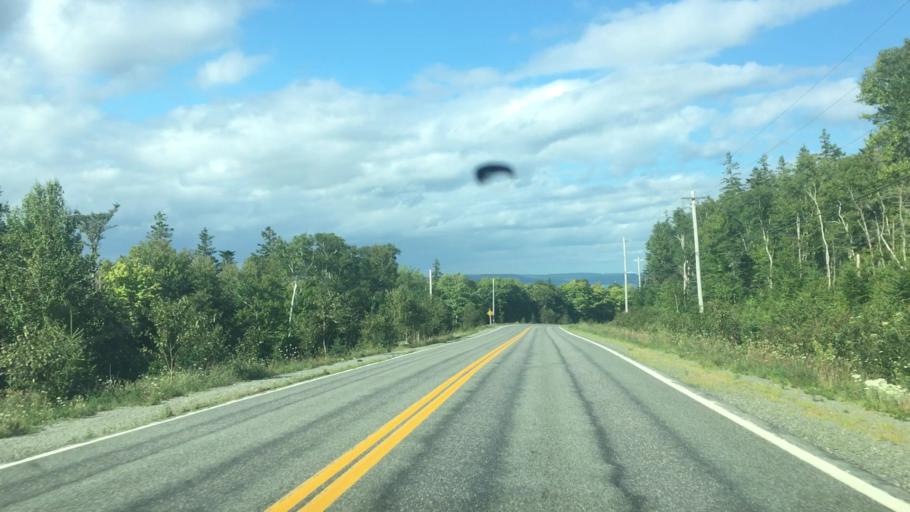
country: CA
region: Nova Scotia
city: Sydney
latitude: 45.8624
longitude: -60.6258
